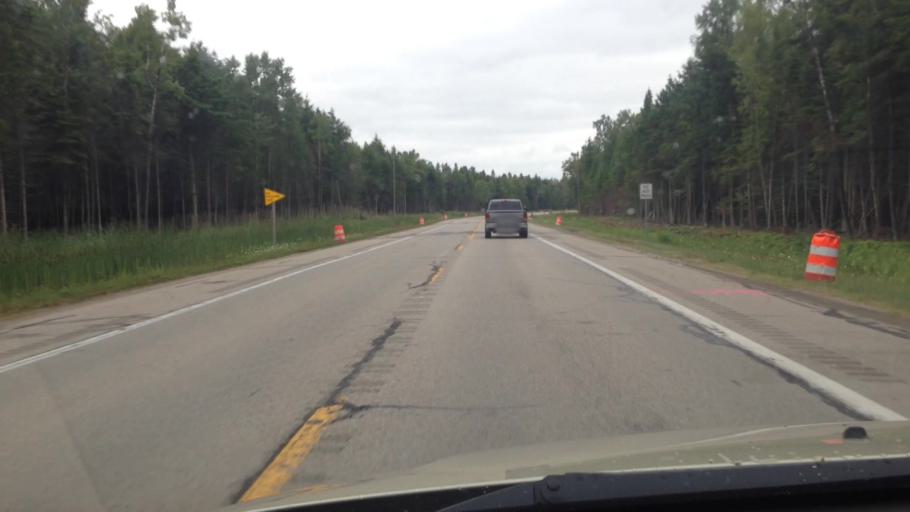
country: US
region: Michigan
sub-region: Delta County
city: Escanaba
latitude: 45.5887
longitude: -87.2379
